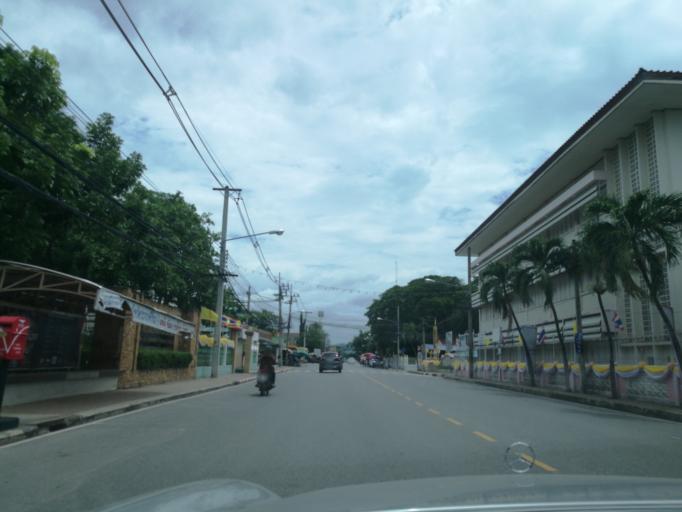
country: TH
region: Prachuap Khiri Khan
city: Prachuap Khiri Khan
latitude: 11.8098
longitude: 99.7972
